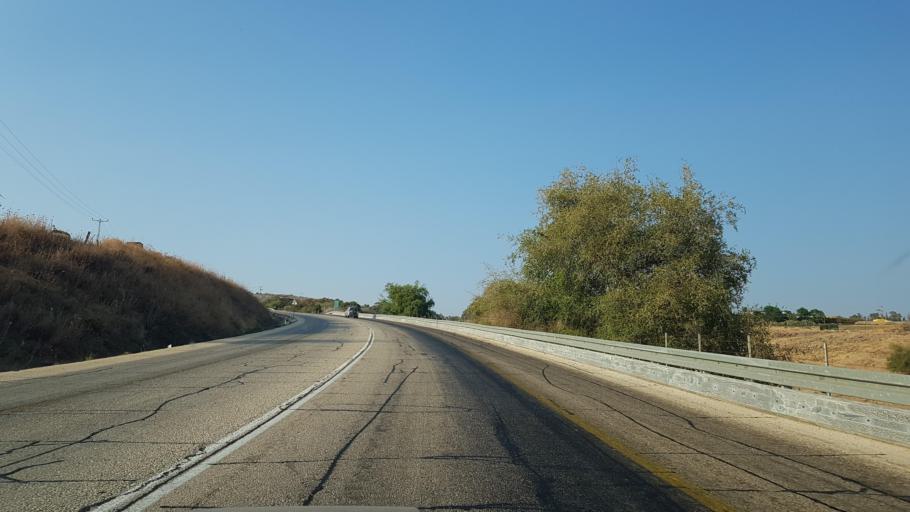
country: SY
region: Quneitra
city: Al Butayhah
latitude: 32.9031
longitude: 35.5978
